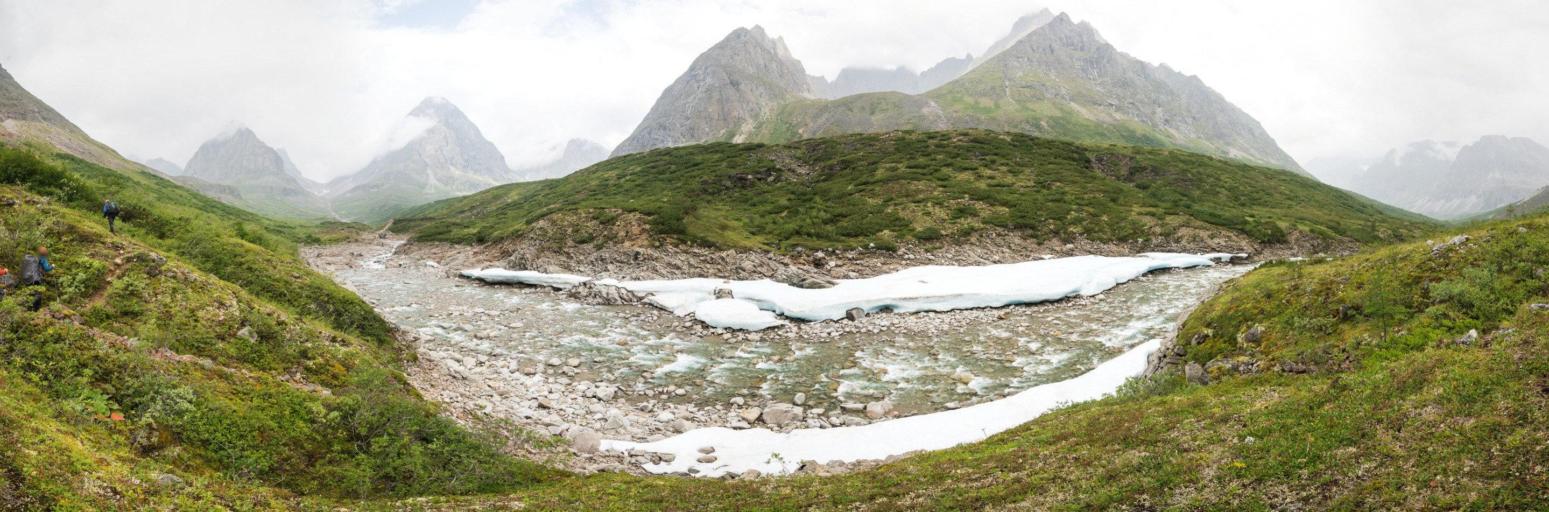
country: RU
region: Transbaikal Territory
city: Chara
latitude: 56.9378
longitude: 117.6197
